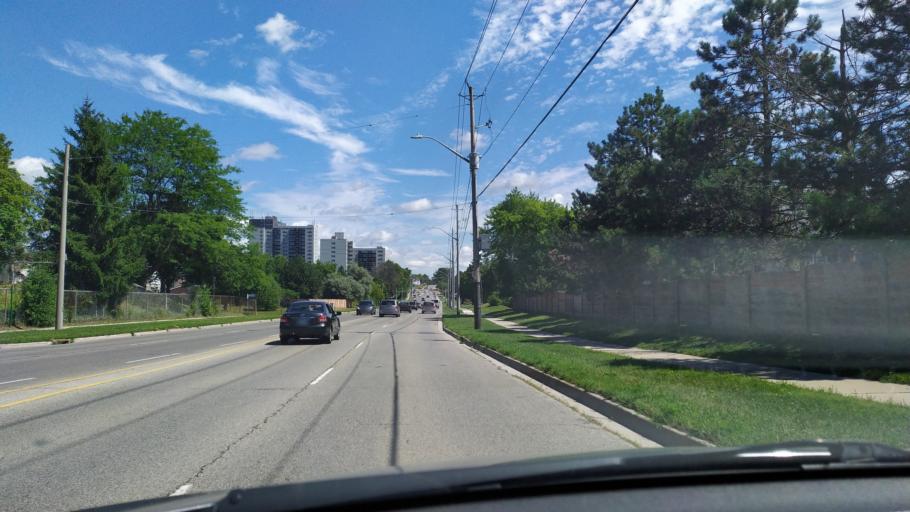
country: CA
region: Ontario
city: Kitchener
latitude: 43.4372
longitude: -80.5271
